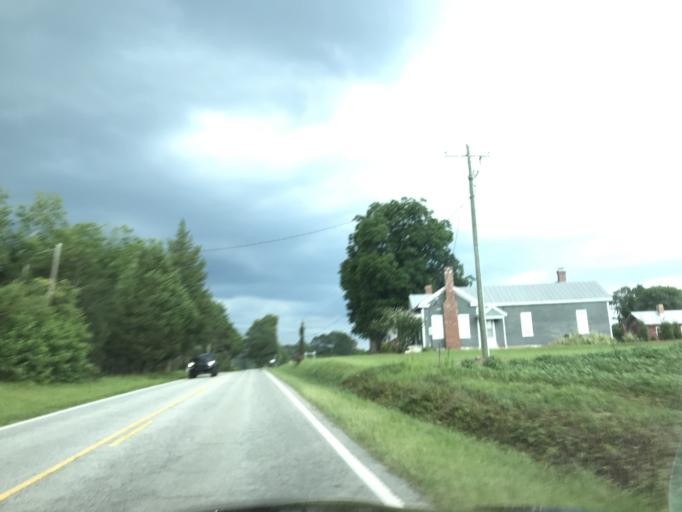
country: US
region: North Carolina
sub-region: Johnston County
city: Four Oaks
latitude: 35.5115
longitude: -78.5103
